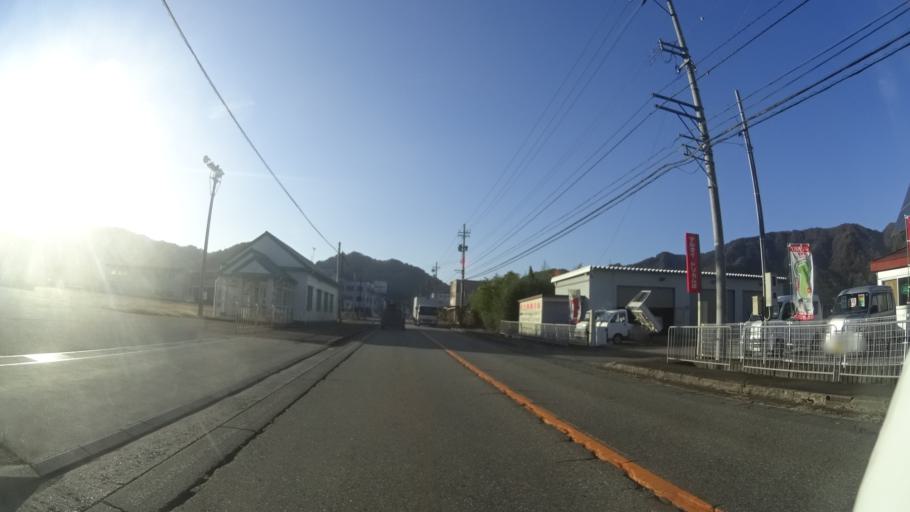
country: JP
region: Fukui
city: Ono
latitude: 35.9932
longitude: 136.4710
